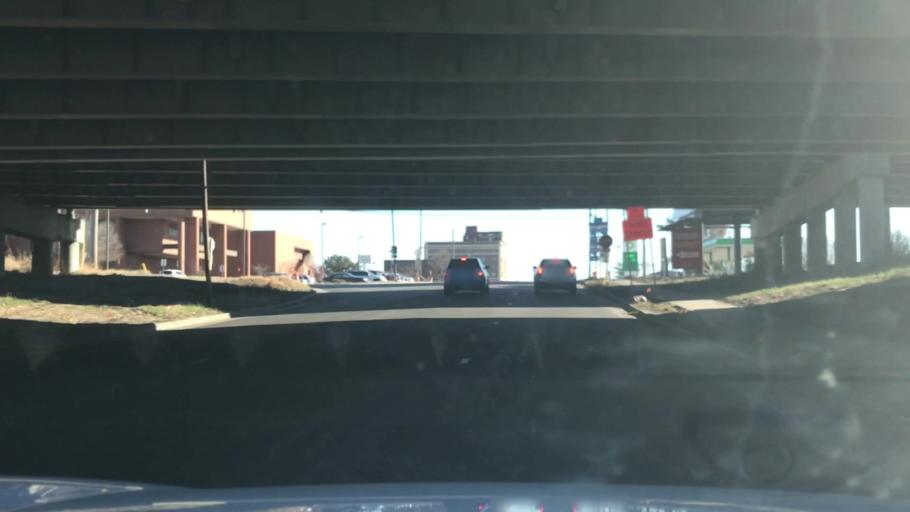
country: US
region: Illinois
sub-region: Saint Clair County
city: East Saint Louis
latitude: 38.6269
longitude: -90.1641
